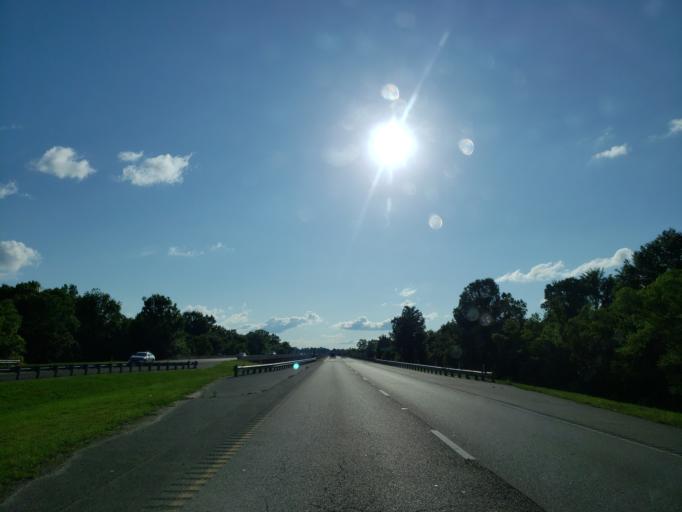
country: US
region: Mississippi
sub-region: Forrest County
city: Petal
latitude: 31.3596
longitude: -89.2787
